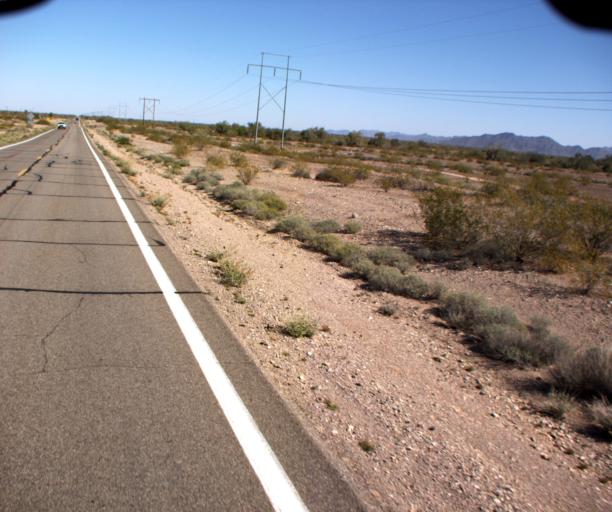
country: US
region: Arizona
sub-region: La Paz County
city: Quartzsite
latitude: 33.4958
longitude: -114.2170
